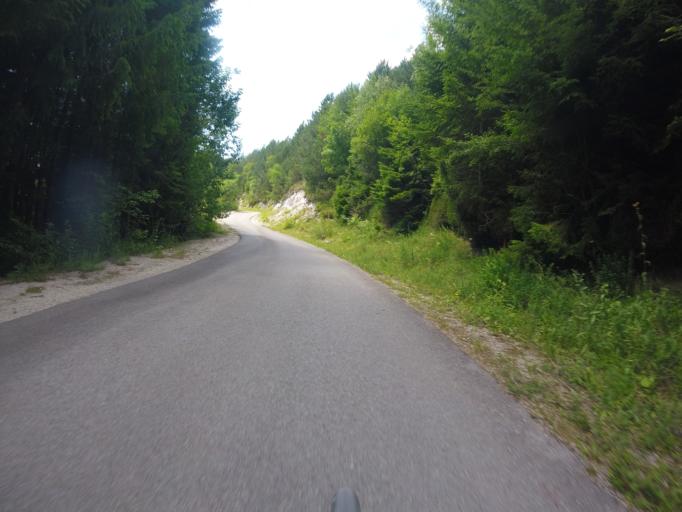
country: SI
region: Kostanjevica na Krki
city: Kostanjevica na Krki
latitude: 45.7623
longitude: 15.3972
